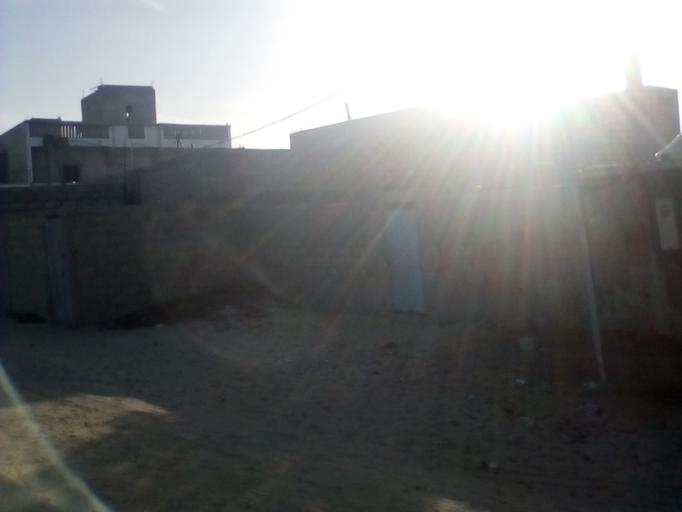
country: SN
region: Saint-Louis
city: Saint-Louis
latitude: 15.9949
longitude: -16.4831
